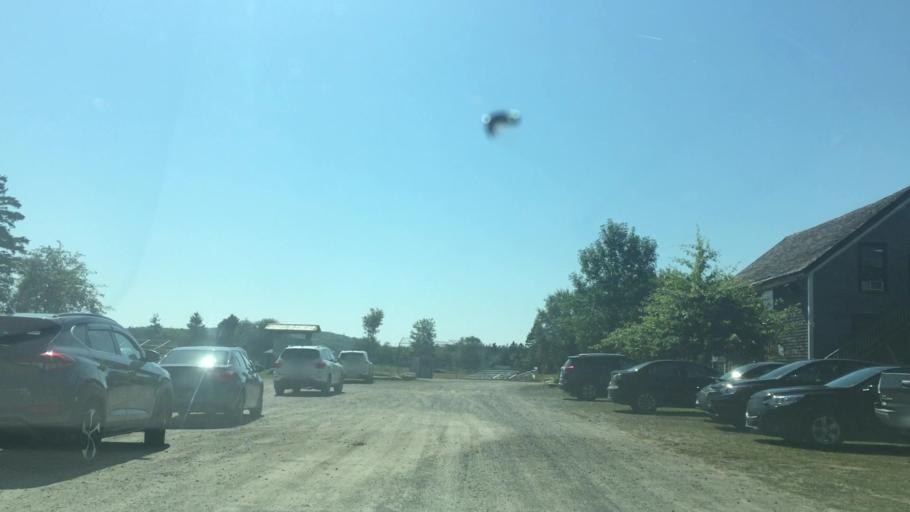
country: CA
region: Nova Scotia
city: Antigonish
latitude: 45.1382
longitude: -61.9830
